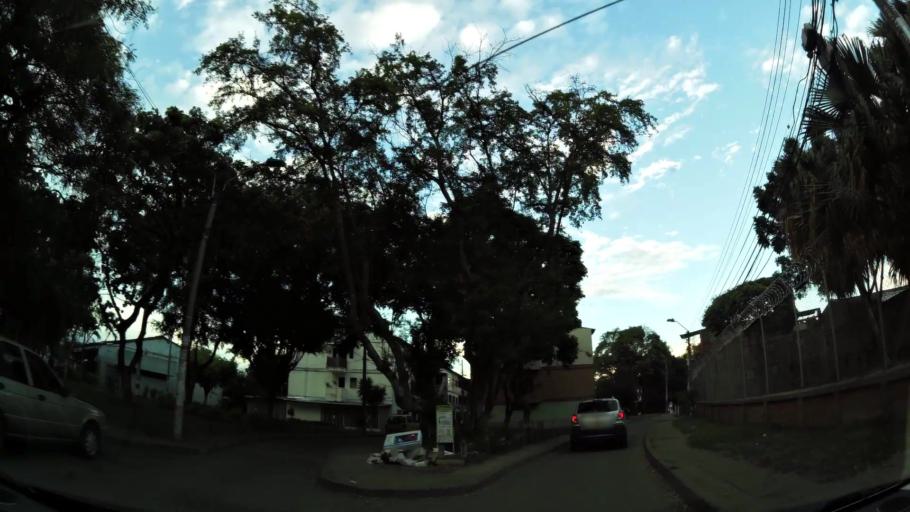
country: CO
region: Valle del Cauca
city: Cali
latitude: 3.4664
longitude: -76.5161
